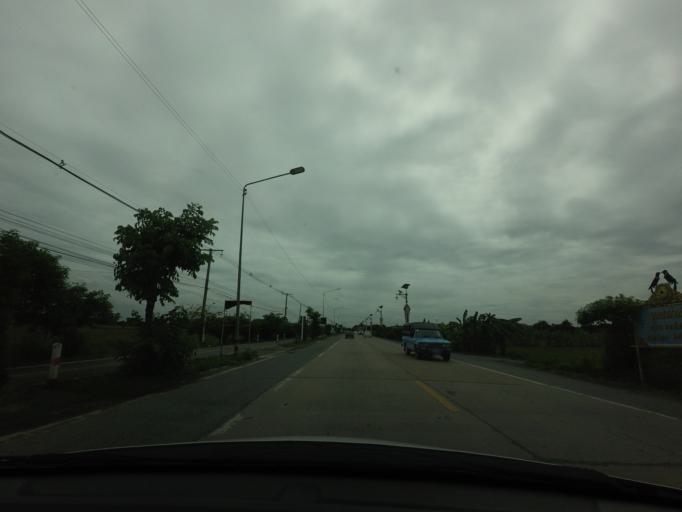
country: TH
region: Pathum Thani
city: Lam Luk Ka
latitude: 13.9298
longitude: 100.7323
